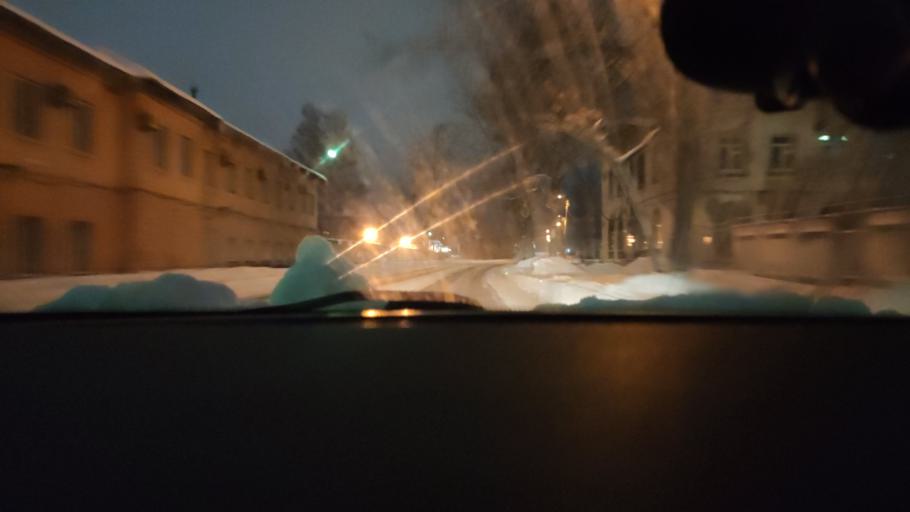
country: RU
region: Perm
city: Krasnokamsk
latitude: 58.0784
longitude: 55.7750
